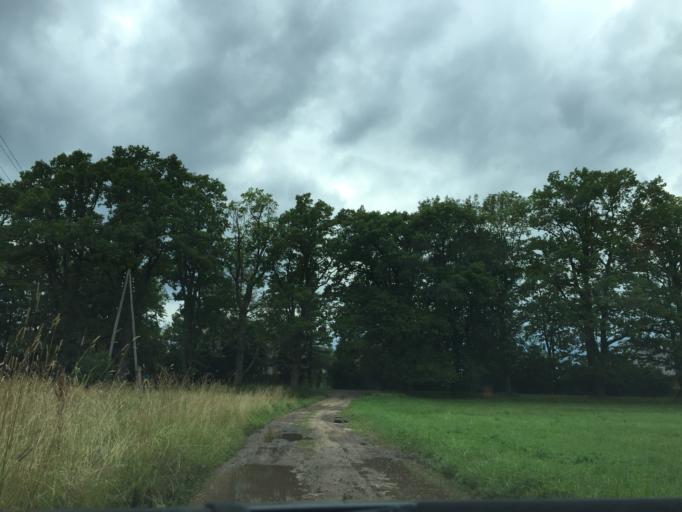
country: LV
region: Seja
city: Loja
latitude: 57.1444
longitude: 24.6637
